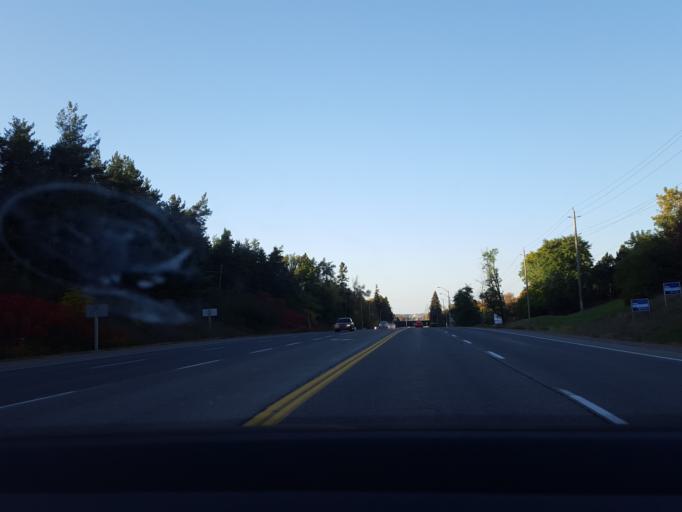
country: CA
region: Ontario
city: Newmarket
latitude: 43.9777
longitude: -79.4623
